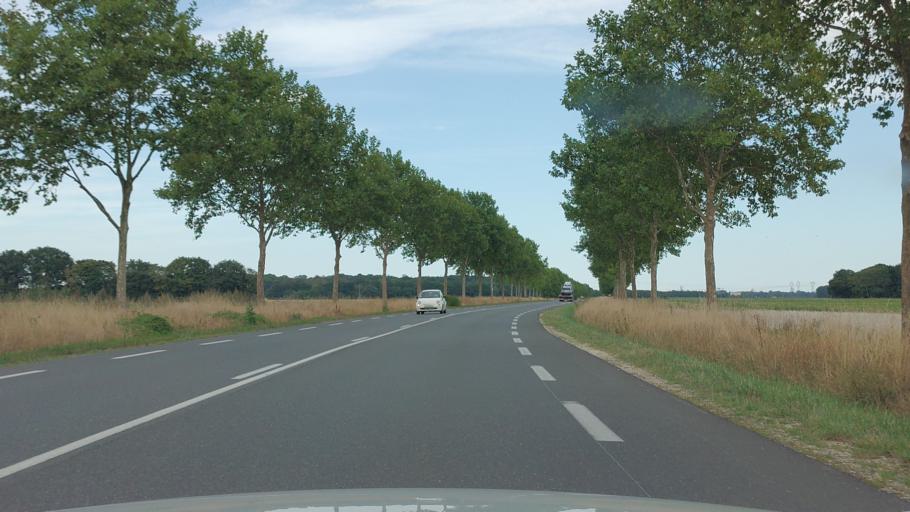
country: FR
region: Ile-de-France
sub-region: Departement de Seine-et-Marne
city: Moisenay
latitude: 48.5466
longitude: 2.7283
